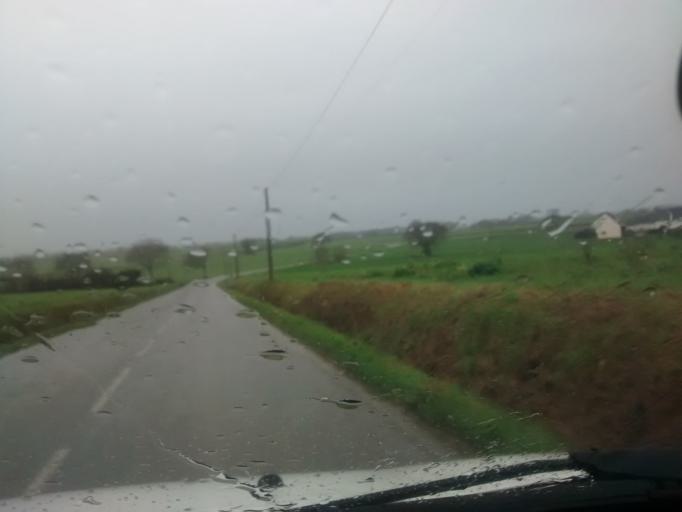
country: FR
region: Brittany
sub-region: Departement d'Ille-et-Vilaine
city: La Gouesniere
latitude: 48.5747
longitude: -1.8892
